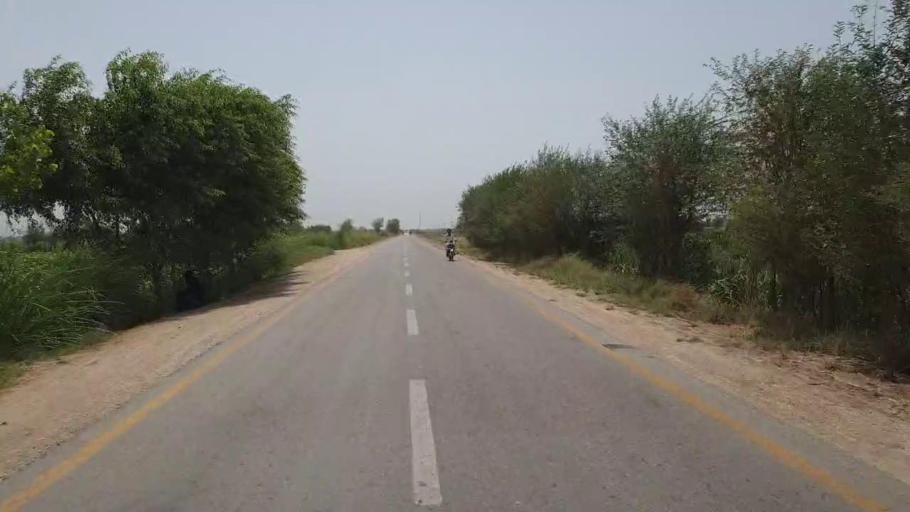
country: PK
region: Sindh
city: Moro
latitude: 26.6003
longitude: 68.0845
